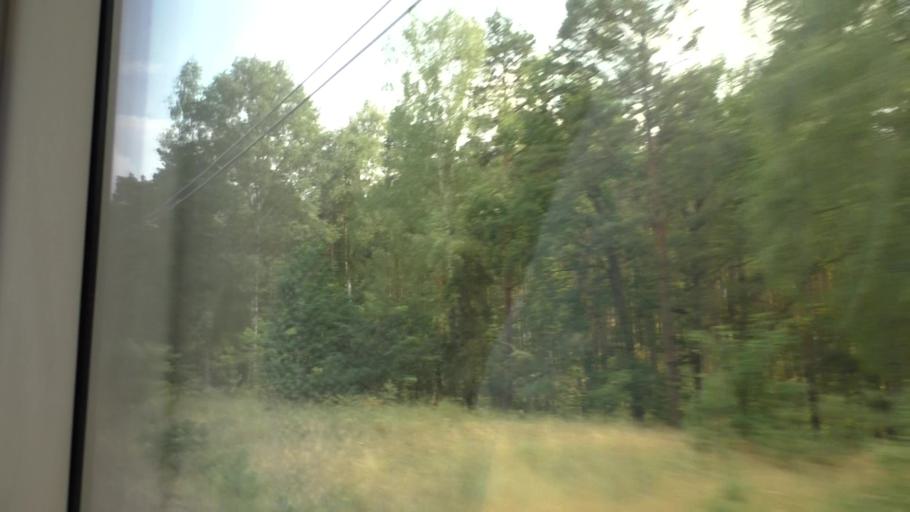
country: DE
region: Brandenburg
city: Wendisch Rietz
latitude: 52.2249
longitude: 13.9768
